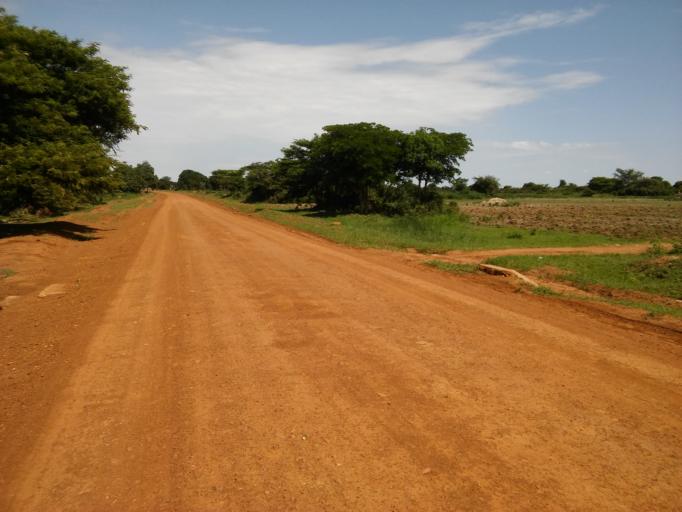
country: UG
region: Eastern Region
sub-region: Kumi District
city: Kumi
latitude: 1.4837
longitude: 33.9105
